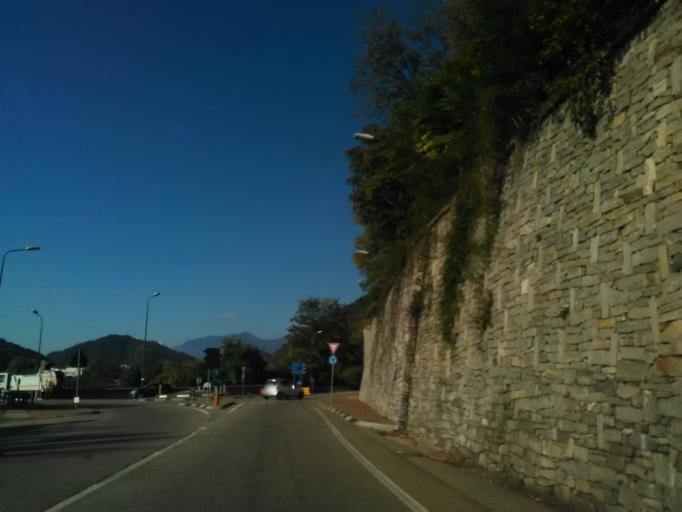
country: IT
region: Piedmont
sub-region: Provincia di Vercelli
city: Borgosesia
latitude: 45.7013
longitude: 8.2878
